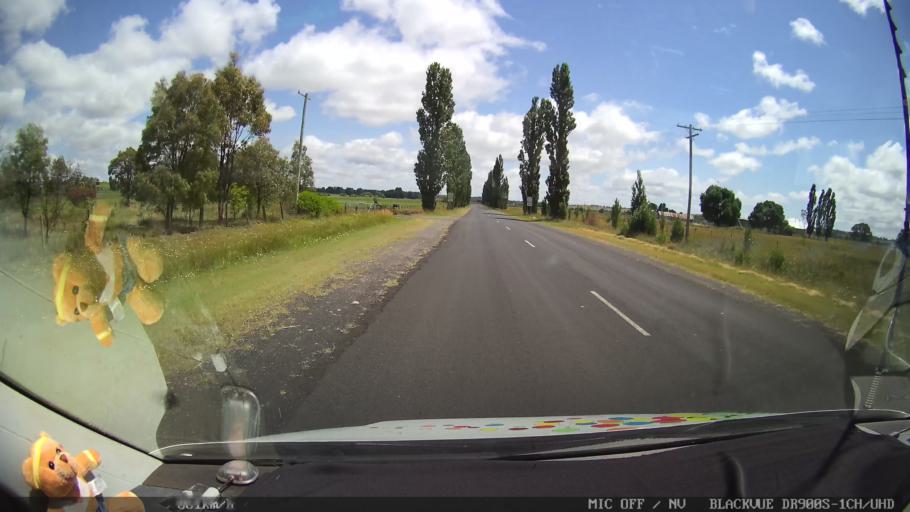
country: AU
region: New South Wales
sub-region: Glen Innes Severn
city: Glen Innes
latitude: -29.7233
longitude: 151.7262
